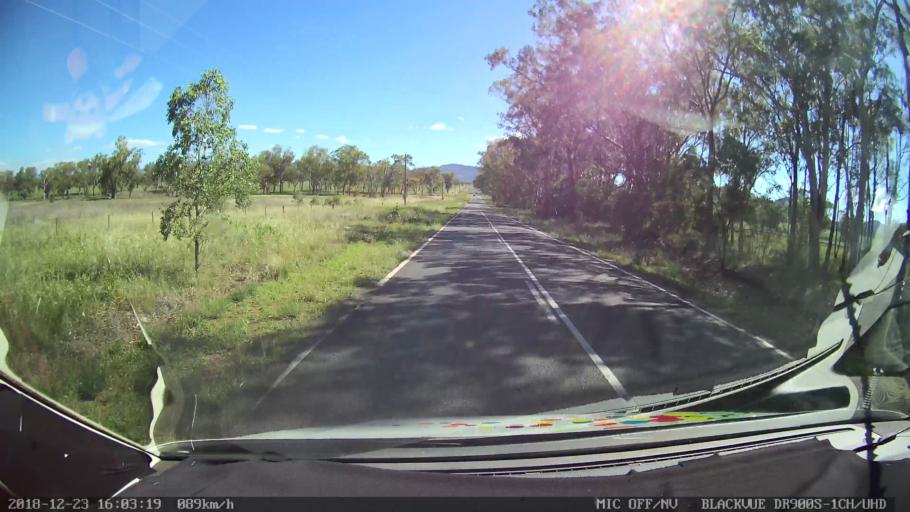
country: AU
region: New South Wales
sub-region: Tamworth Municipality
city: Phillip
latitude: -31.2421
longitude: 150.8017
